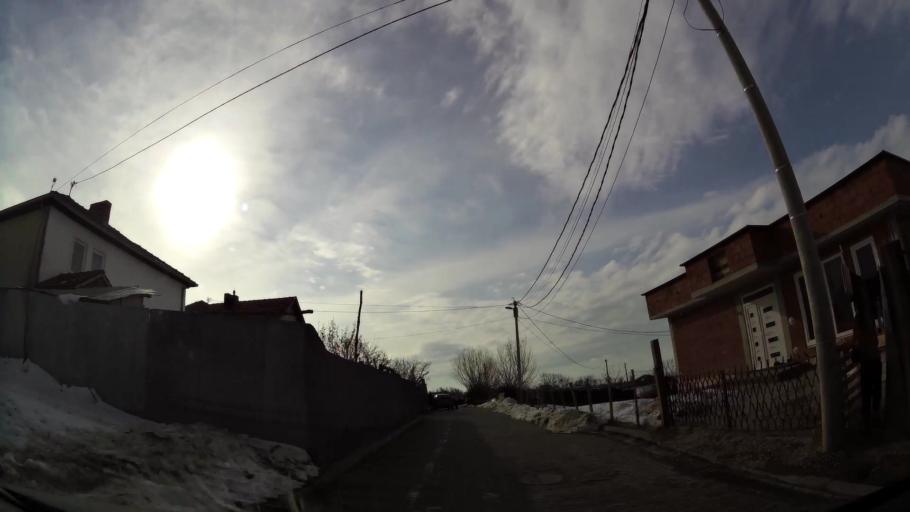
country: XK
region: Pristina
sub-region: Komuna e Prishtines
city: Pristina
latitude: 42.6762
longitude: 21.1527
